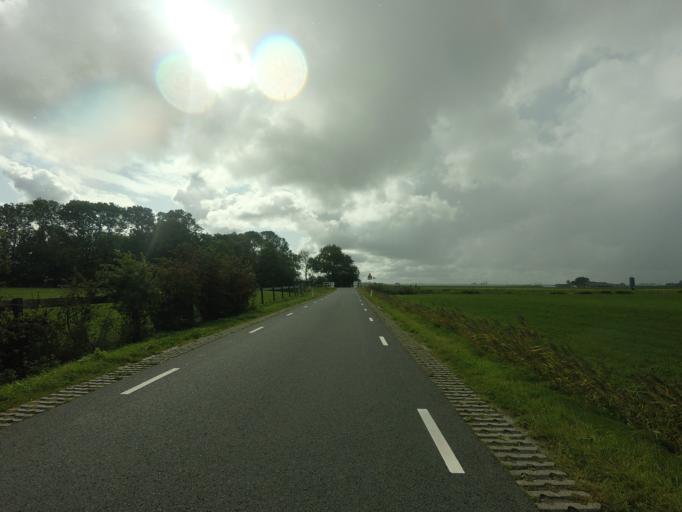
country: NL
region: Friesland
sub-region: Gemeente Boarnsterhim
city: Wergea
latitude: 53.1488
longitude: 5.8344
